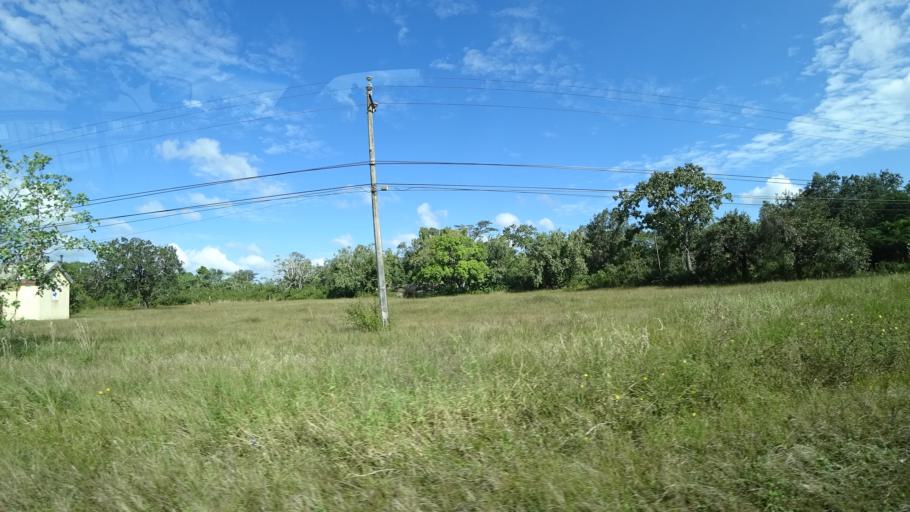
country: BZ
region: Belize
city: Belize City
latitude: 17.5692
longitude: -88.4010
